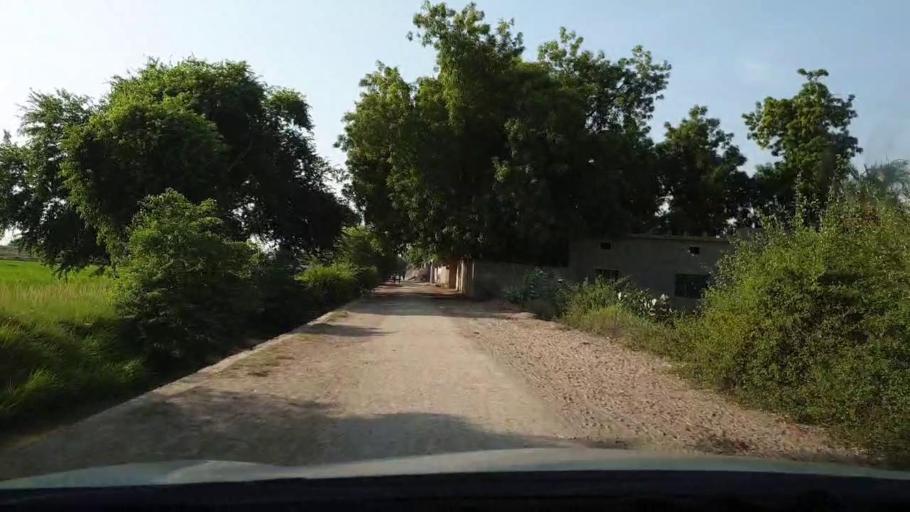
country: PK
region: Sindh
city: Larkana
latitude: 27.5496
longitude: 68.2665
